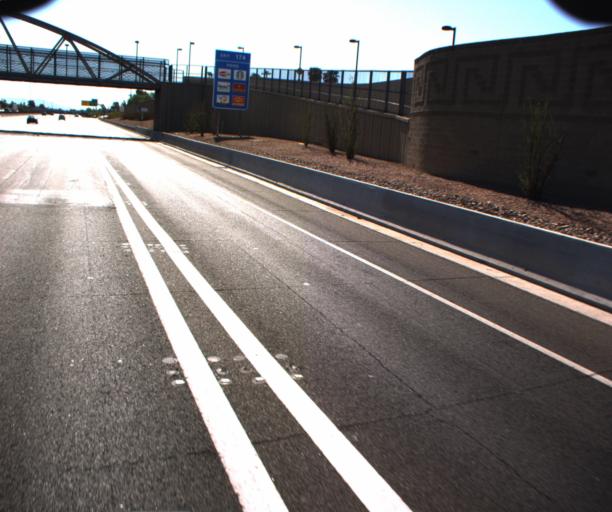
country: US
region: Arizona
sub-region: Maricopa County
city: Tempe Junction
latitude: 33.3854
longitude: -111.9349
